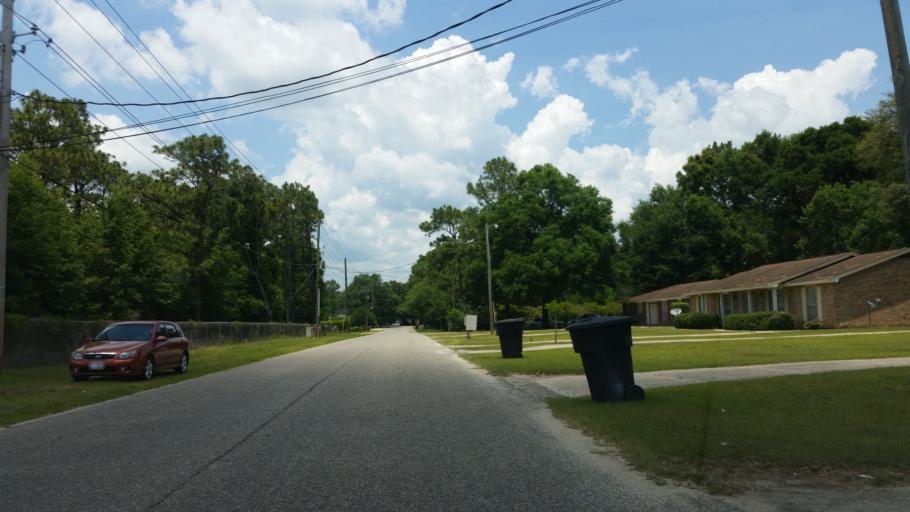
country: US
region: Florida
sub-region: Escambia County
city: Ferry Pass
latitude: 30.4983
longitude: -87.2049
